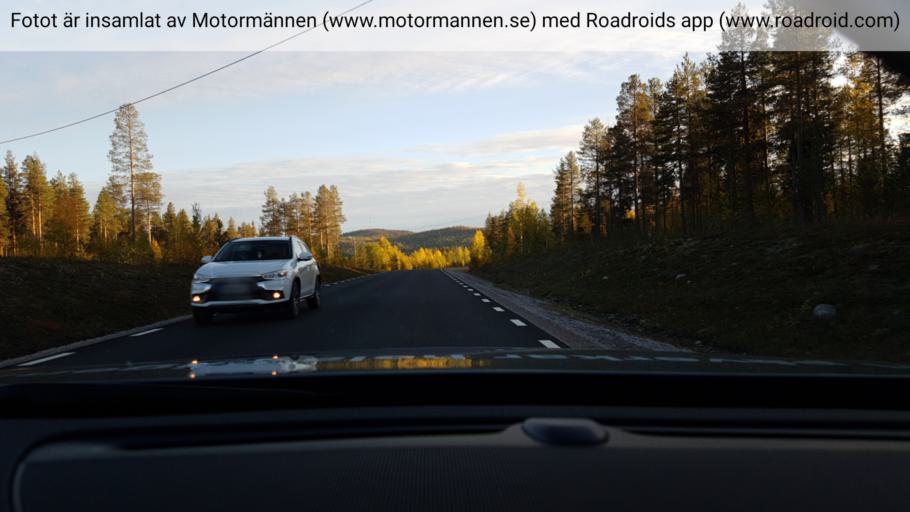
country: SE
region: Norrbotten
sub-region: Jokkmokks Kommun
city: Jokkmokk
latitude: 66.5803
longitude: 19.8051
